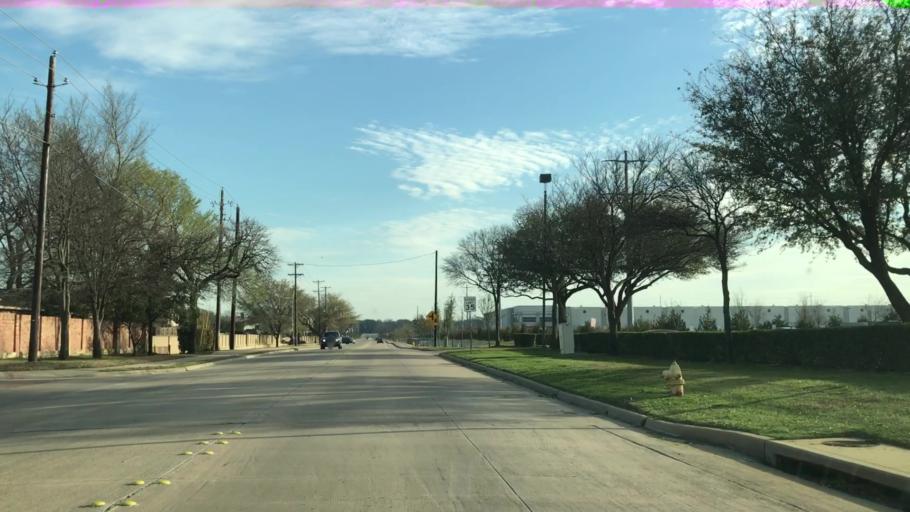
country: US
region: Texas
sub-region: Dallas County
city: Coppell
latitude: 32.9814
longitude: -97.0113
